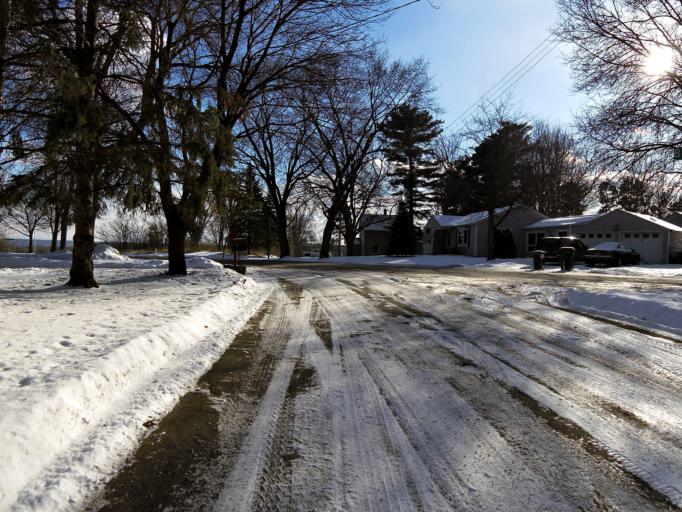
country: US
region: Minnesota
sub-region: Washington County
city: Oak Park Heights
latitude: 45.0386
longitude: -92.7986
